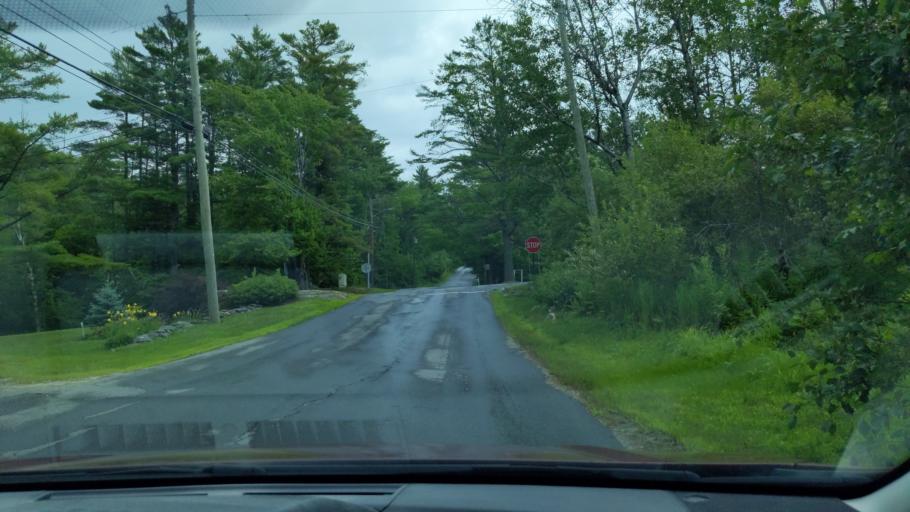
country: US
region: New Hampshire
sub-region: Merrimack County
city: New London
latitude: 43.4134
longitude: -72.0083
